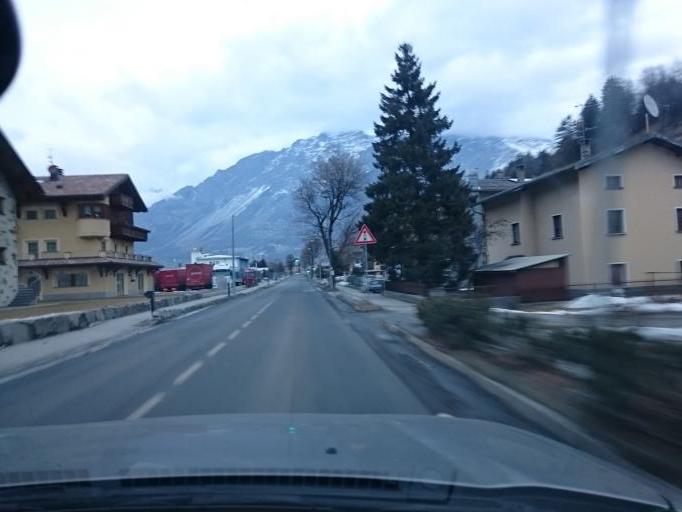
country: IT
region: Lombardy
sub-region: Provincia di Sondrio
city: Cepina
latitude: 46.4426
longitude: 10.3598
